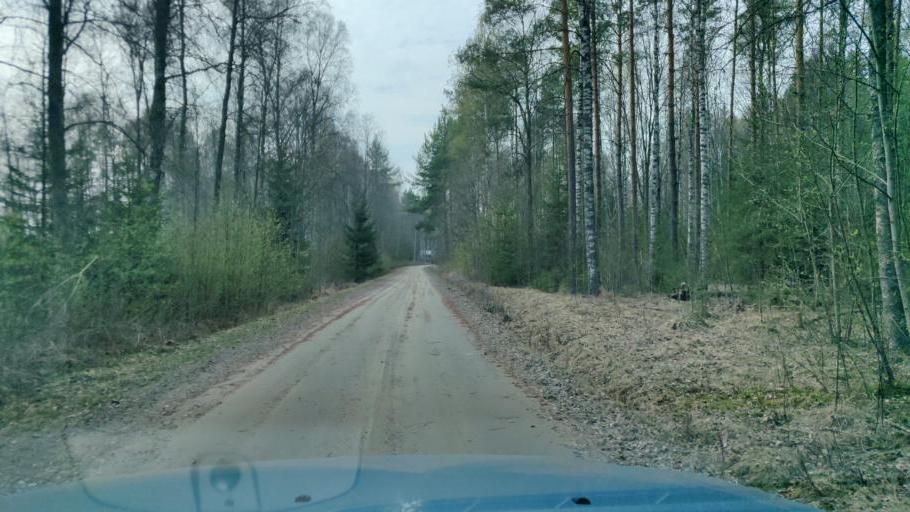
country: SE
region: Vaermland
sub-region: Munkfors Kommun
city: Munkfors
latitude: 59.8742
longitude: 13.5517
